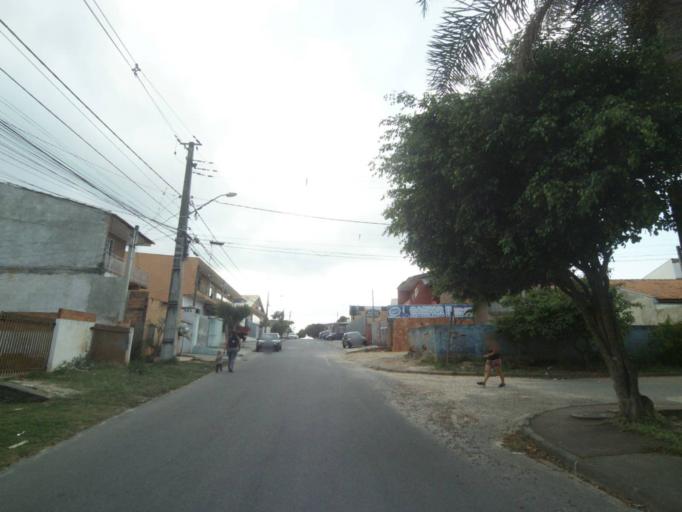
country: BR
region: Parana
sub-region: Sao Jose Dos Pinhais
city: Sao Jose dos Pinhais
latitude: -25.5493
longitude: -49.2559
